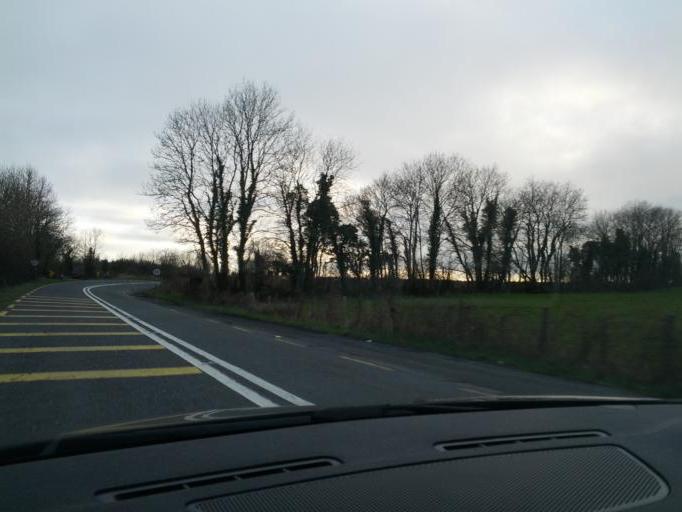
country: IE
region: Connaught
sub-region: Sligo
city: Ballymote
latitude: 54.1368
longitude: -8.5555
